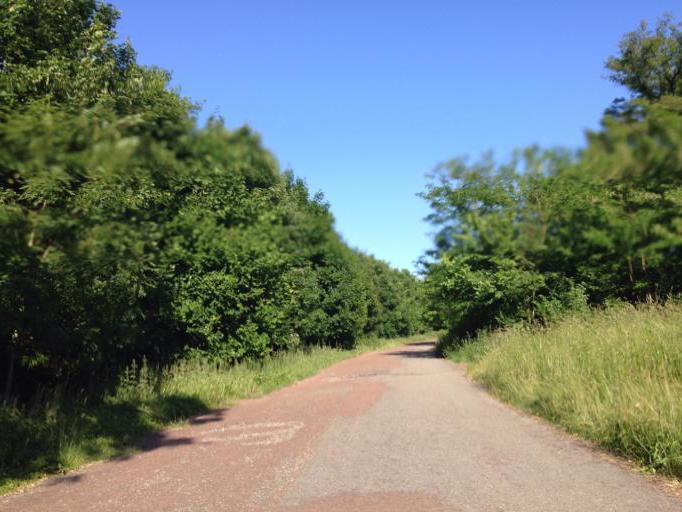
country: FR
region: Ile-de-France
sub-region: Departement des Hauts-de-Seine
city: Clamart
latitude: 48.7935
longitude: 2.2475
